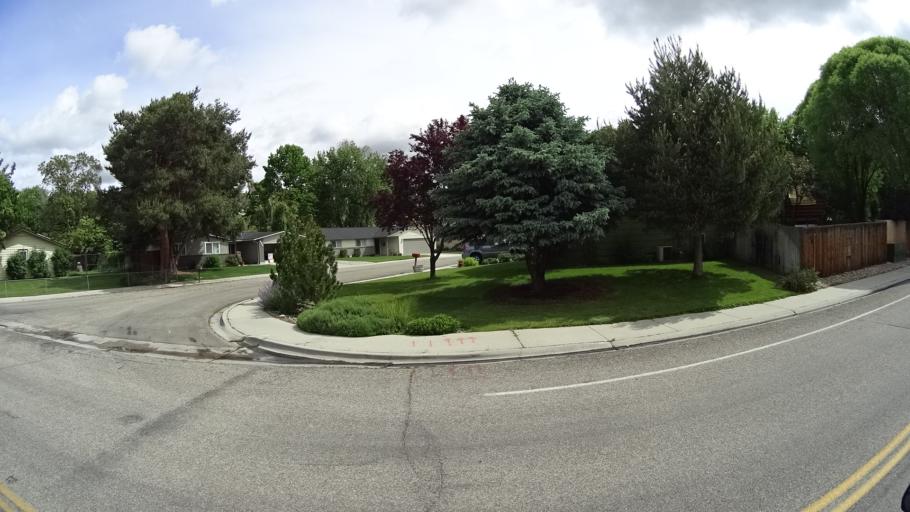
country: US
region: Idaho
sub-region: Ada County
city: Eagle
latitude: 43.6978
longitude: -116.3491
